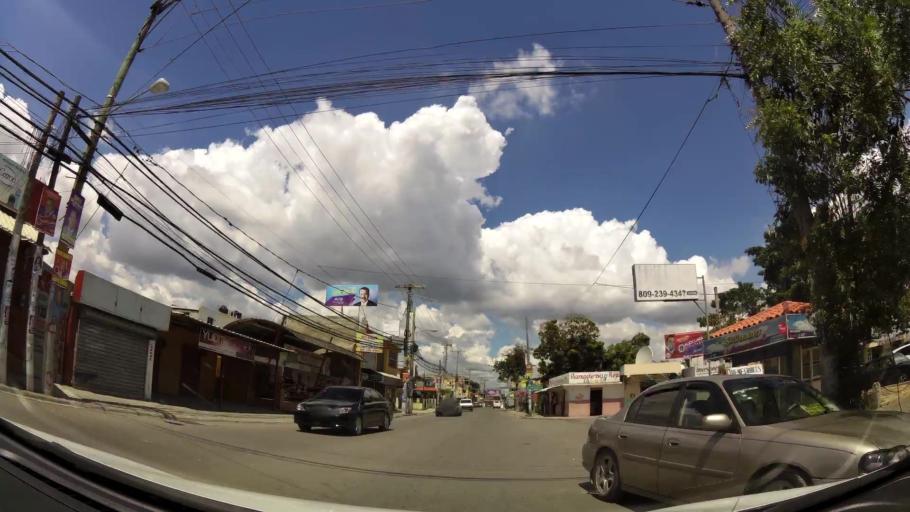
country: DO
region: Santo Domingo
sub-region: Santo Domingo
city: Santo Domingo Este
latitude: 18.5338
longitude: -69.8657
